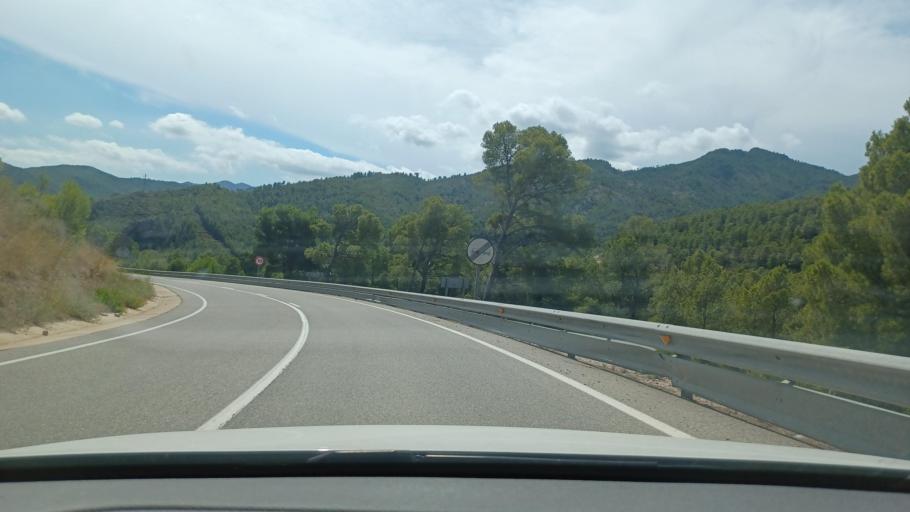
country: ES
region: Catalonia
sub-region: Provincia de Tarragona
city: Benifallet
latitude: 40.9702
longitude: 0.4455
